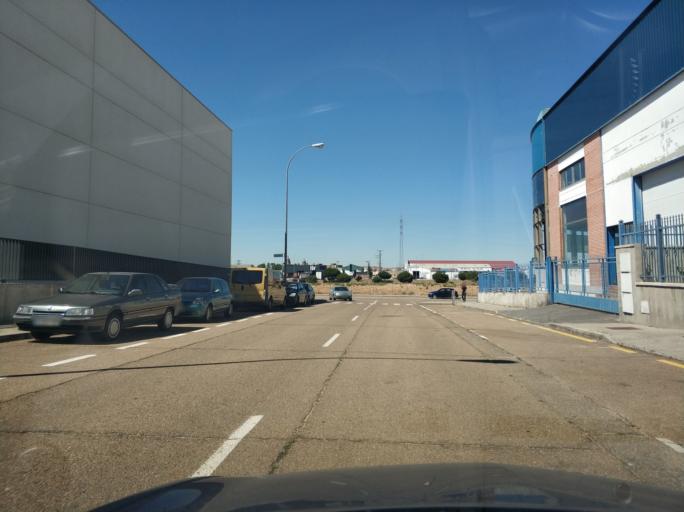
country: ES
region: Castille and Leon
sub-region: Provincia de Salamanca
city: Carbajosa de la Sagrada
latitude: 40.9404
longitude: -5.6582
